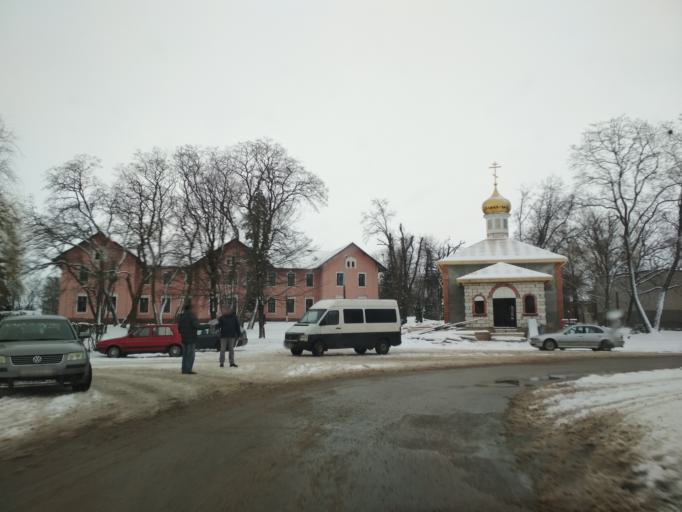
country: BY
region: Minsk
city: Mar''ina Horka
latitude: 53.5329
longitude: 28.1212
